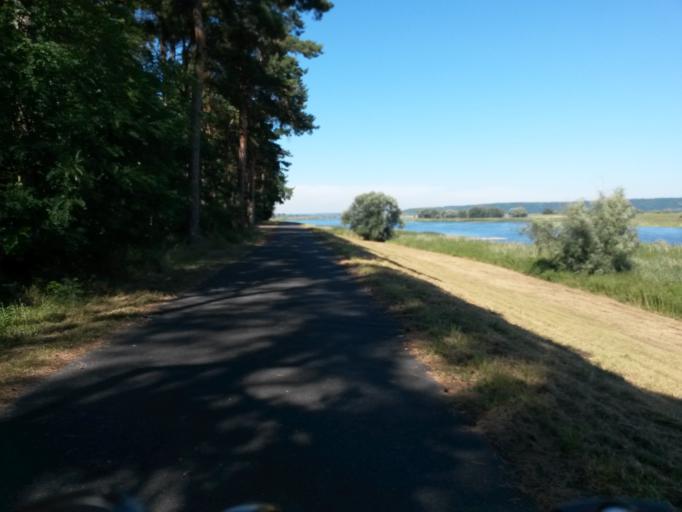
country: PL
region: West Pomeranian Voivodeship
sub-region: Powiat gryfinski
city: Cedynia
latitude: 52.8901
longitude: 14.1573
